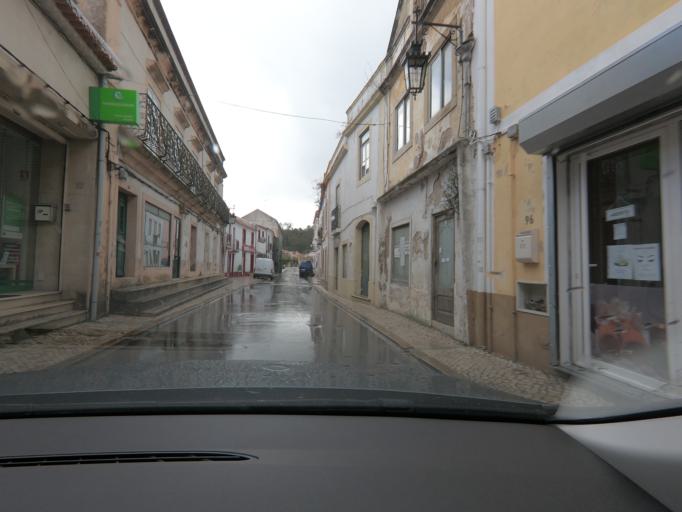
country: PT
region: Lisbon
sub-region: Alenquer
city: Alenquer
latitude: 39.0547
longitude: -9.0077
